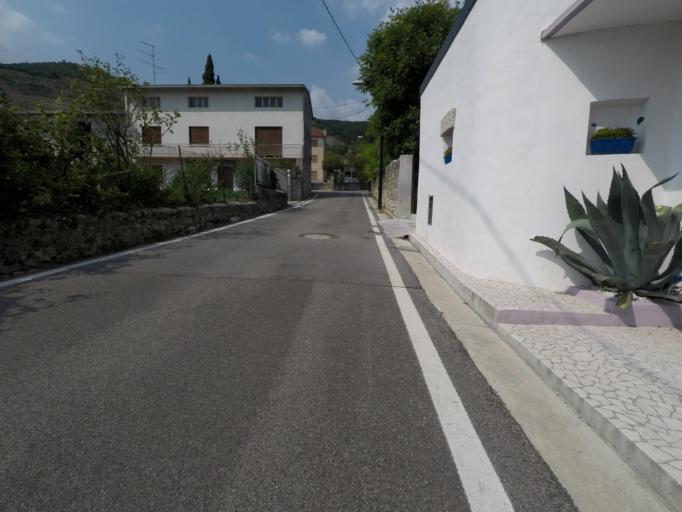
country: IT
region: Friuli Venezia Giulia
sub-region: Provincia di Pordenone
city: Caneva
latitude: 45.9679
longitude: 12.4298
